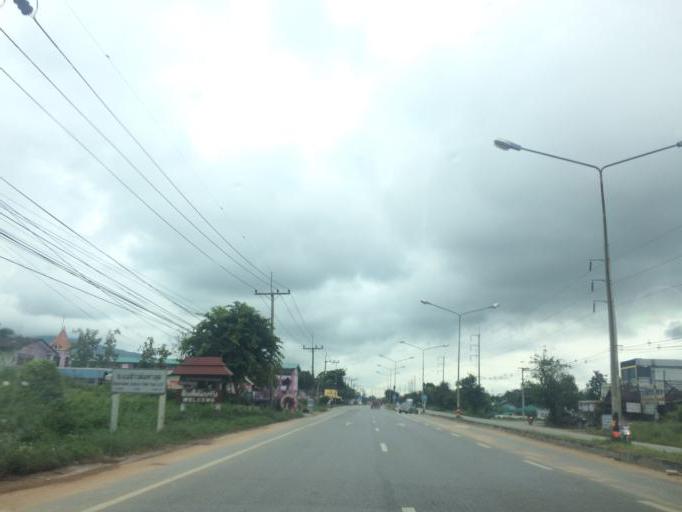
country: TH
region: Chiang Rai
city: Mae Chan
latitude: 20.0696
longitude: 99.8755
